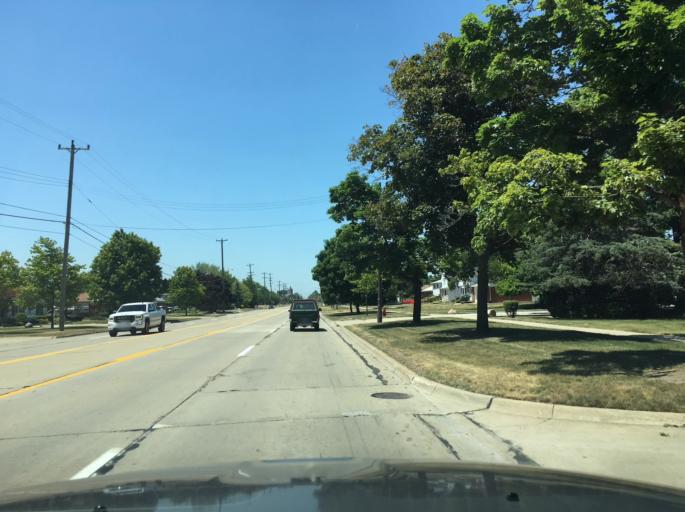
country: US
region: Michigan
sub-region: Macomb County
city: Fraser
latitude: 42.5391
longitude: -82.9431
